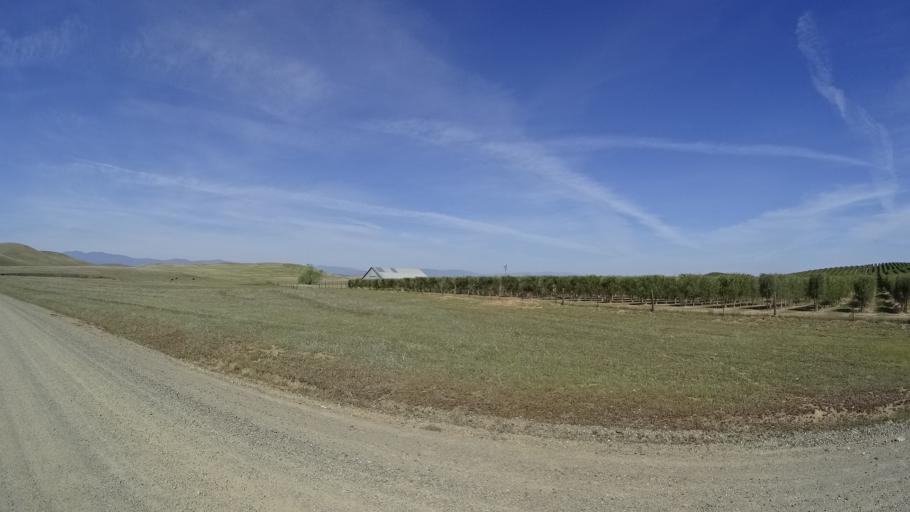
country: US
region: California
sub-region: Glenn County
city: Willows
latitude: 39.6150
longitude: -122.2939
